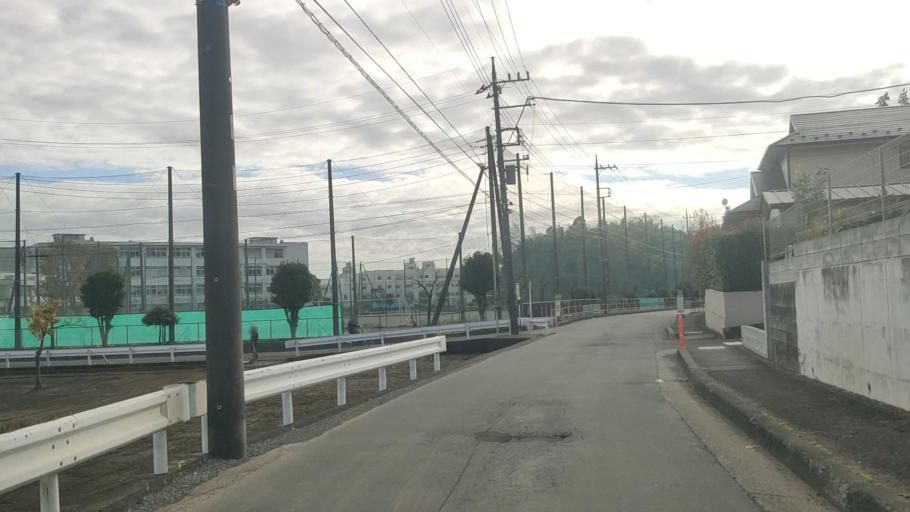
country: JP
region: Kanagawa
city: Minami-rinkan
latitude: 35.4803
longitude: 139.4681
